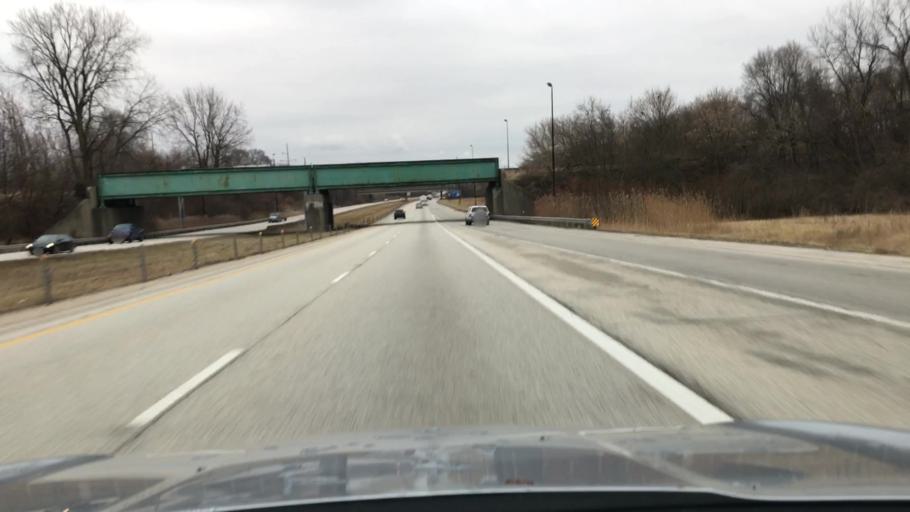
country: US
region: Illinois
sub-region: Sangamon County
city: Grandview
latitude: 39.8285
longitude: -89.5931
